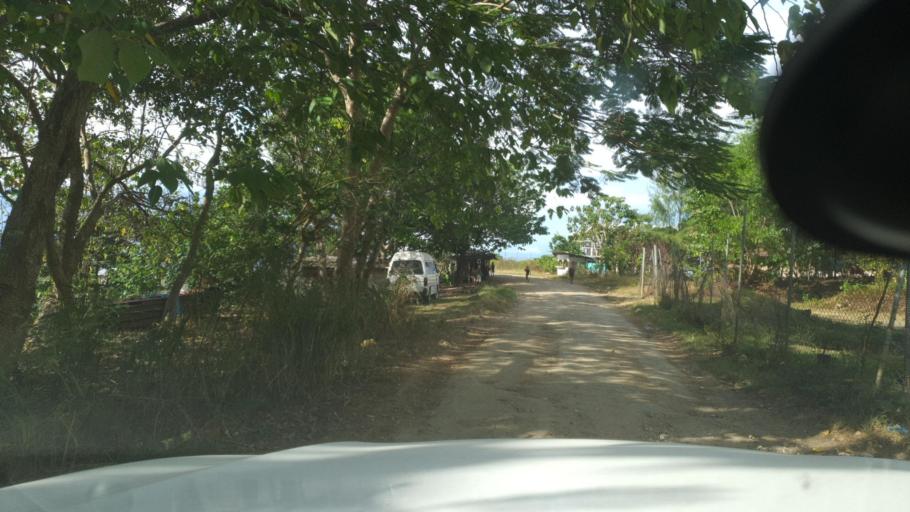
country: SB
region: Guadalcanal
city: Honiara
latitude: -9.4447
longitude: 159.9365
